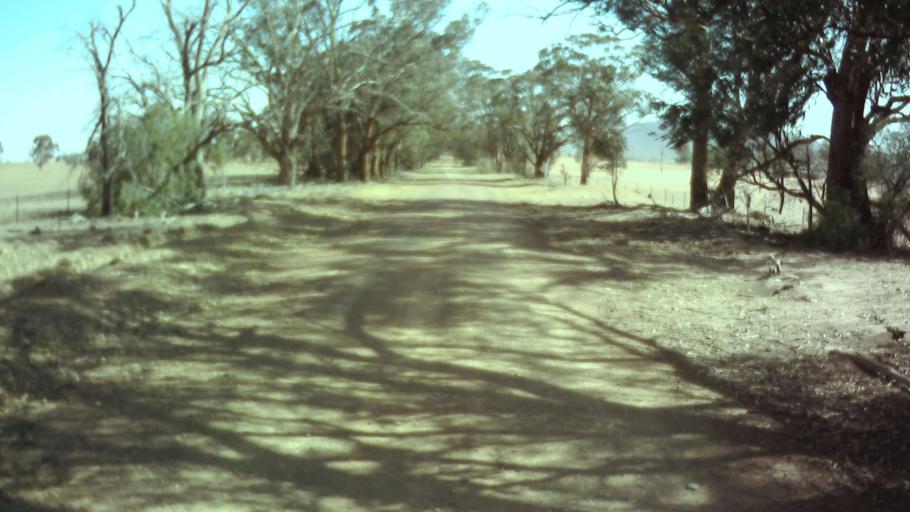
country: AU
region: New South Wales
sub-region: Weddin
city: Grenfell
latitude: -33.8428
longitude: 148.0178
